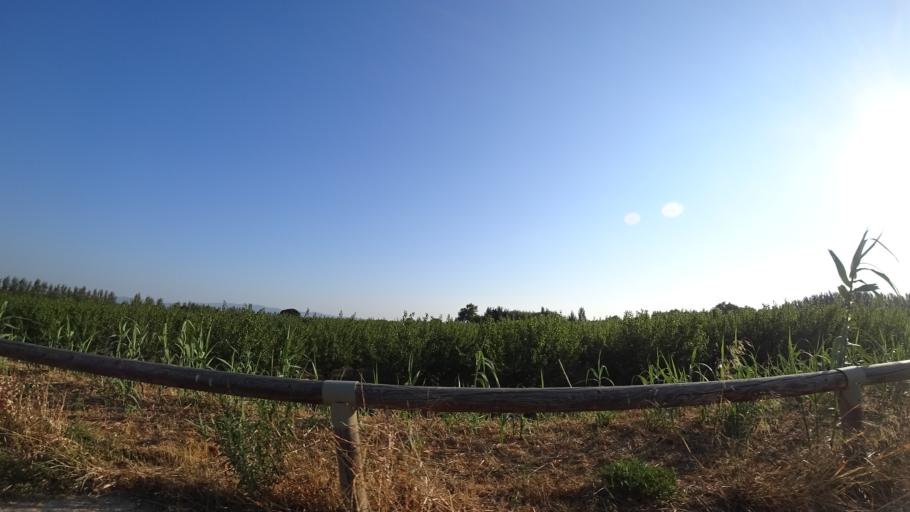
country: FR
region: Languedoc-Roussillon
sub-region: Departement des Pyrenees-Orientales
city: Pia
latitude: 42.7611
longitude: 2.9241
